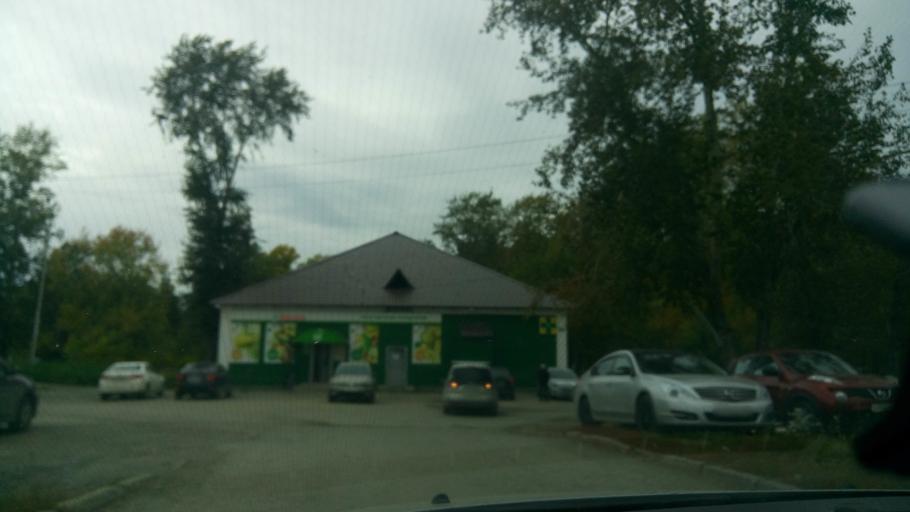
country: RU
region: Sverdlovsk
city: Sovkhoznyy
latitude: 56.7782
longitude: 60.5917
